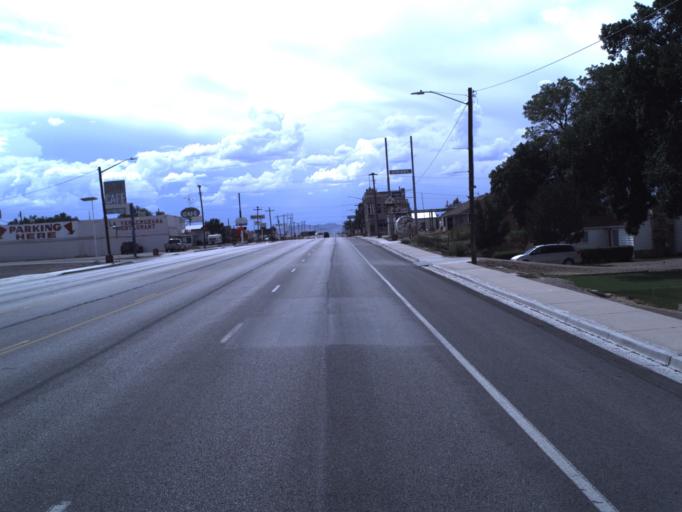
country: US
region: Utah
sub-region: Carbon County
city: East Carbon City
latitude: 38.9956
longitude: -110.1628
